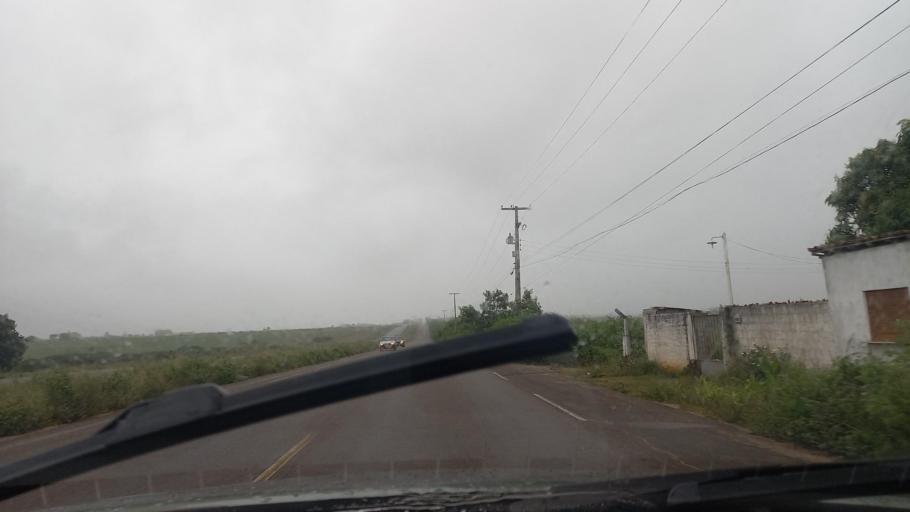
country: BR
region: Alagoas
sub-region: Lagoa Da Canoa
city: Lagoa da Canoa
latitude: -9.6967
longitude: -36.8099
